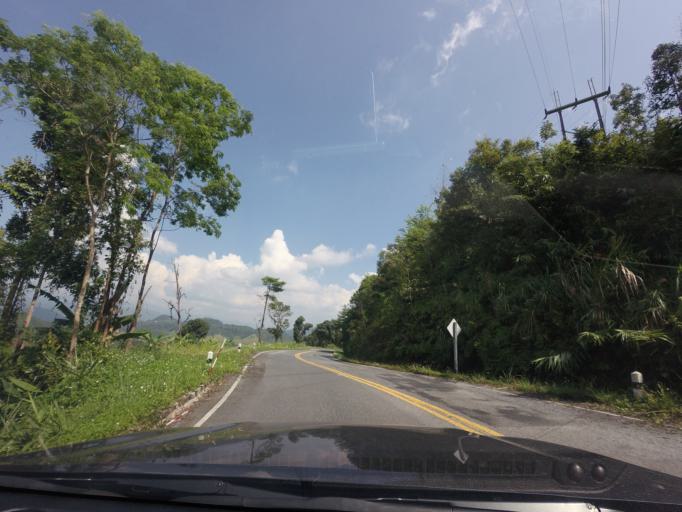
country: TH
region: Nan
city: Bo Kluea
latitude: 19.0541
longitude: 101.0894
